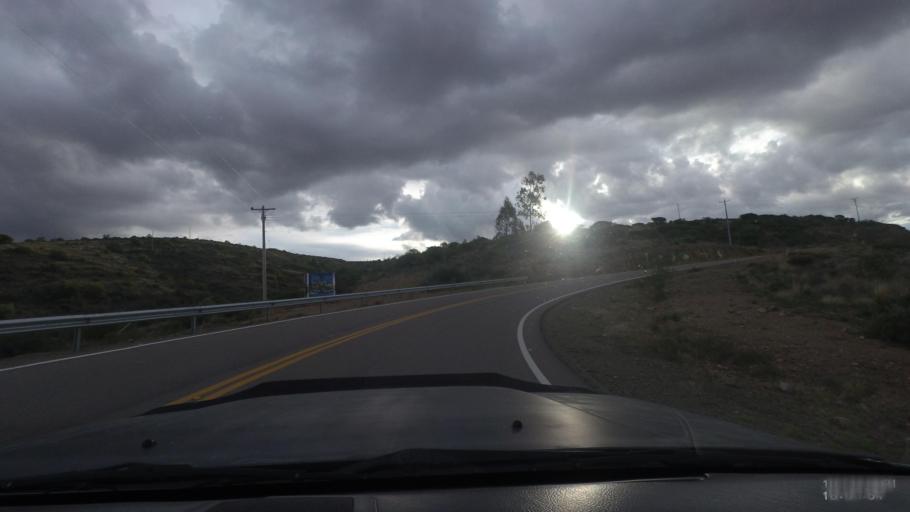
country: BO
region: Cochabamba
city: Cliza
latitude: -17.7517
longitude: -65.9163
